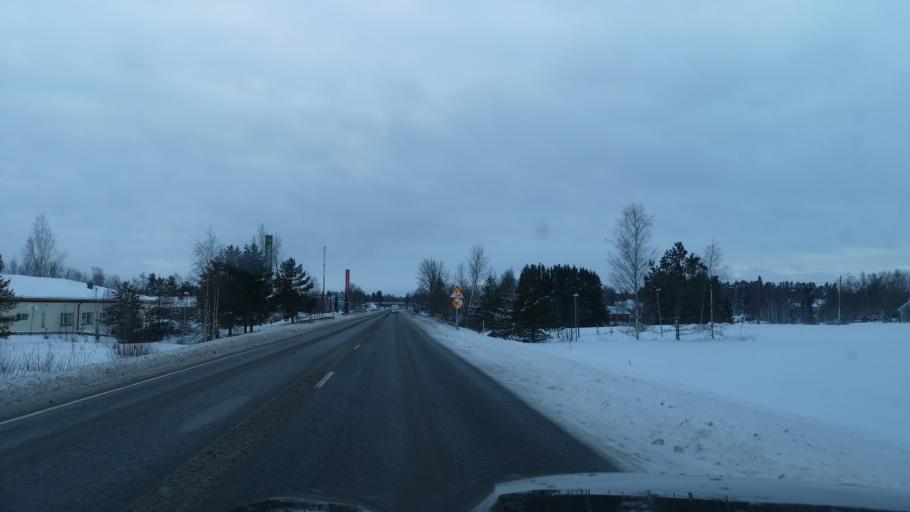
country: FI
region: Varsinais-Suomi
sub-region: Loimaa
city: Loimaa
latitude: 60.8599
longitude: 23.0459
